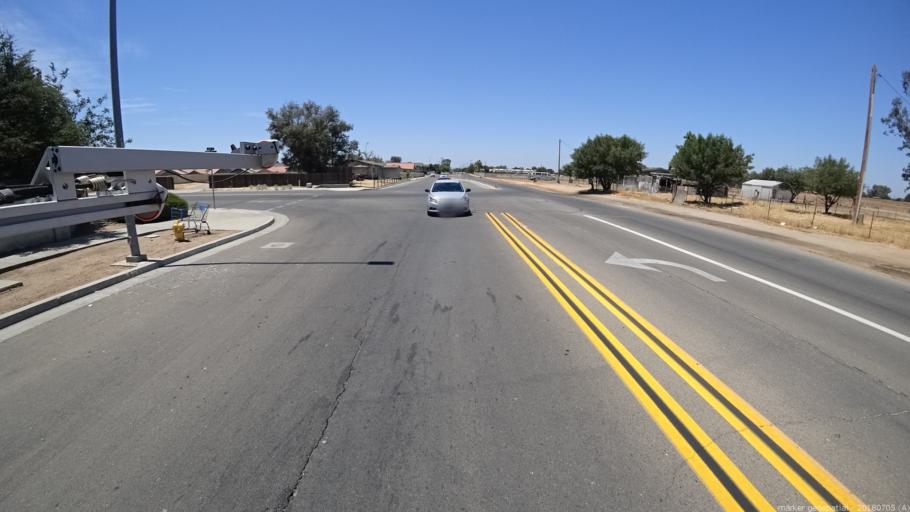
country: US
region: California
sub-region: Madera County
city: Madera
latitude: 36.9867
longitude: -120.0522
